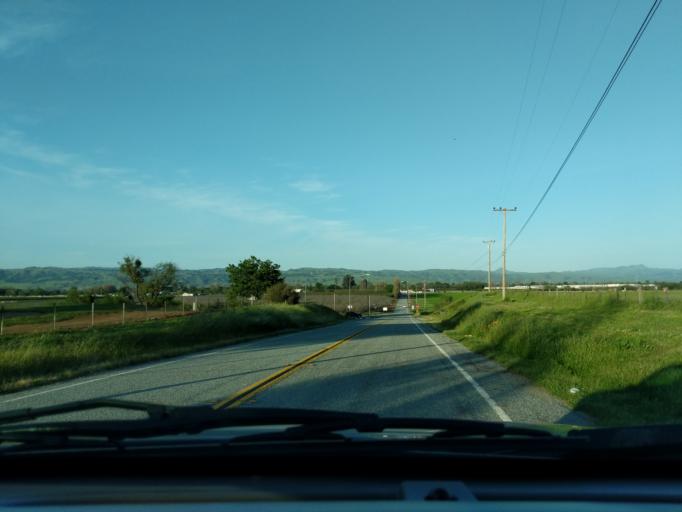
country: US
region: California
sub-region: Santa Clara County
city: Gilroy
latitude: 36.9659
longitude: -121.5632
